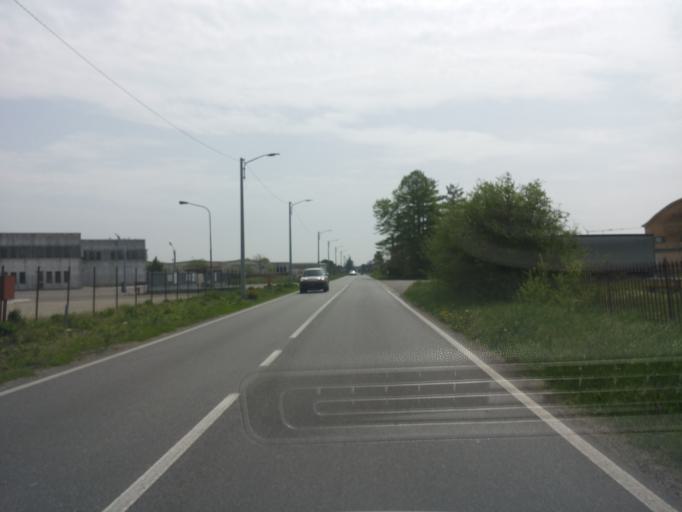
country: IT
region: Piedmont
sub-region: Provincia di Alessandria
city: Occimiano
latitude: 45.0716
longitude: 8.4905
